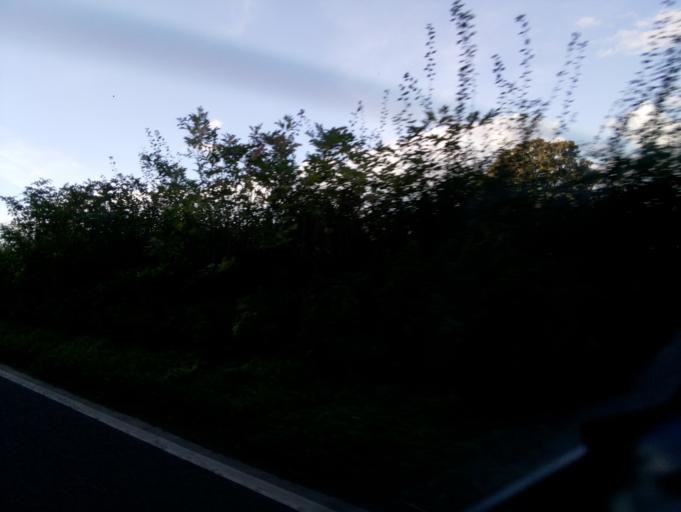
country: GB
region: England
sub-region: Herefordshire
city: Clifford
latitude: 52.1179
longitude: -3.0583
